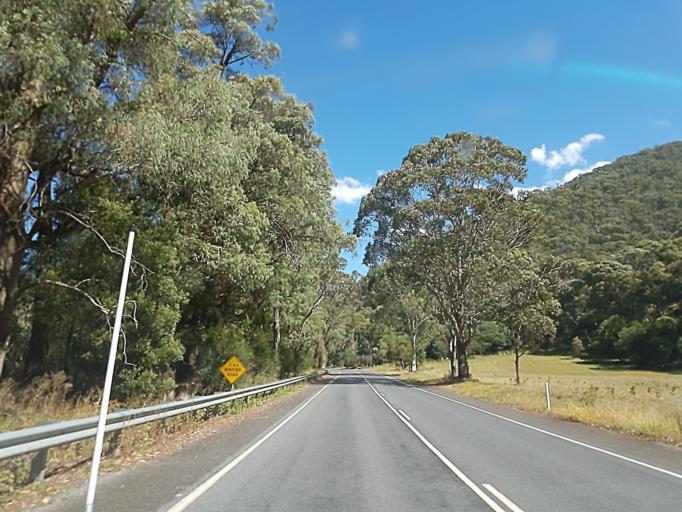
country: AU
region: Victoria
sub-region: Alpine
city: Mount Beauty
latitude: -36.8433
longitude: 147.0783
